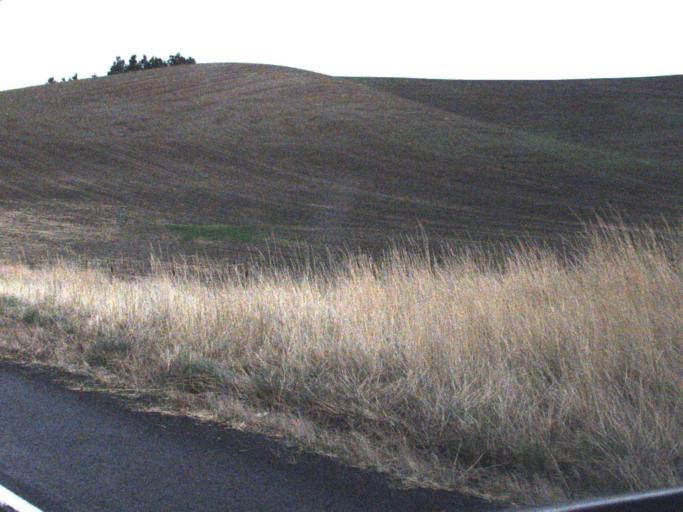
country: US
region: Washington
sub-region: Columbia County
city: Dayton
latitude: 46.3785
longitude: -117.9403
